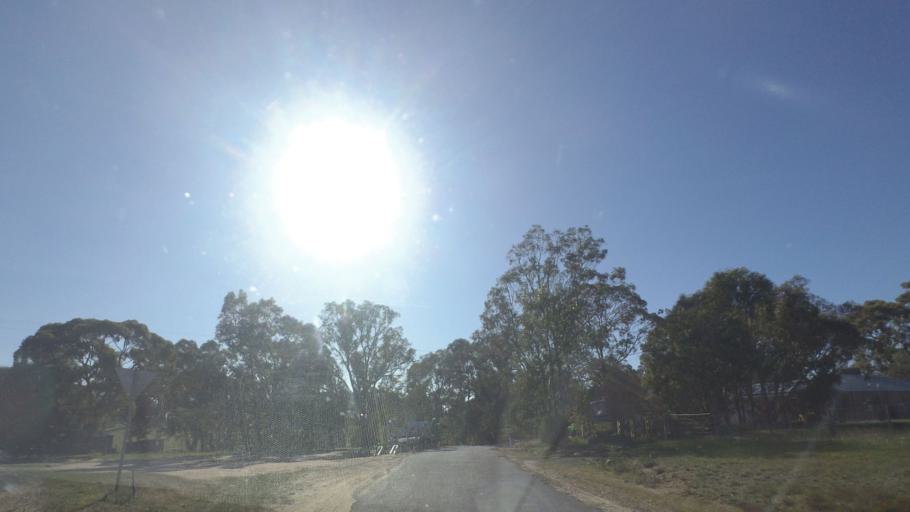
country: AU
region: Victoria
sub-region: Mount Alexander
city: Castlemaine
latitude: -37.1074
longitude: 144.4198
